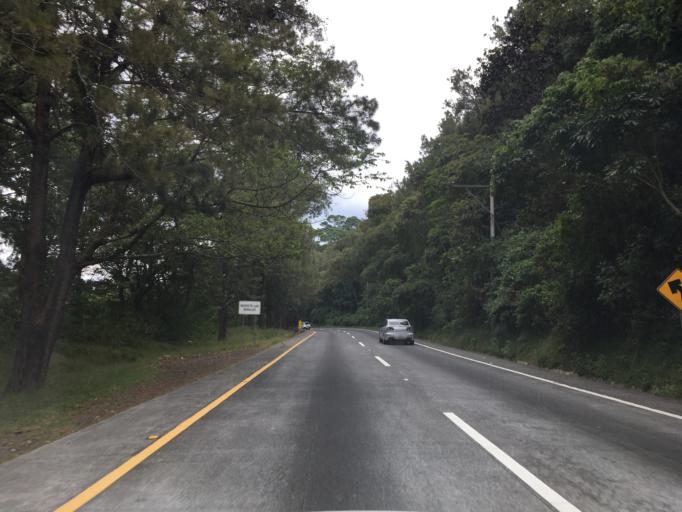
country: GT
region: Sacatepequez
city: Santa Lucia Milpas Altas
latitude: 14.5669
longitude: -90.6822
